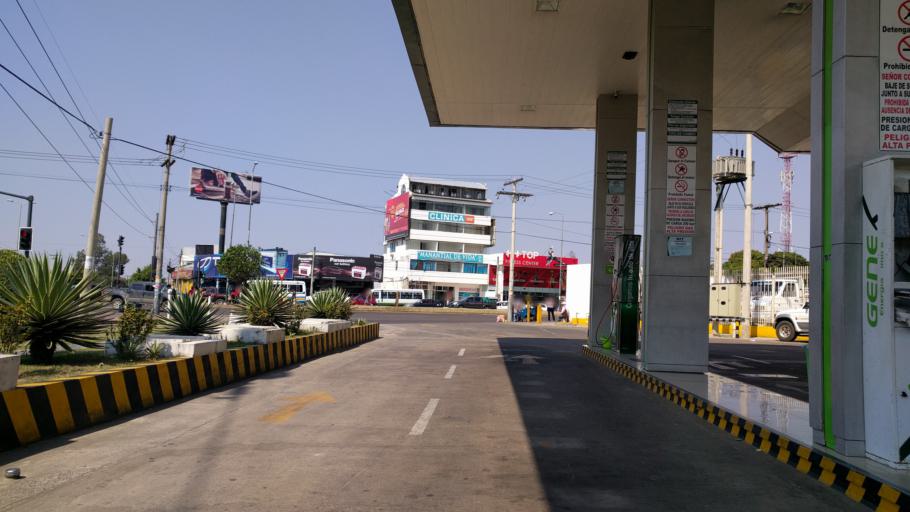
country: BO
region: Santa Cruz
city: Santa Cruz de la Sierra
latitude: -17.8036
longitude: -63.1998
